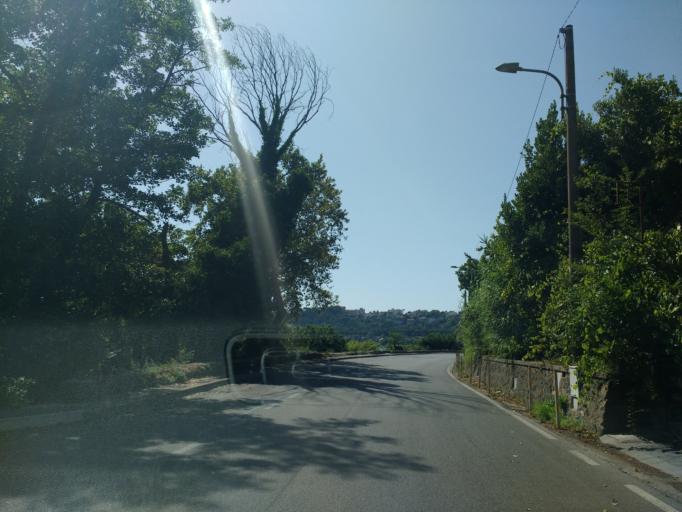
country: IT
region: Latium
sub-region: Citta metropolitana di Roma Capitale
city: Castel Gandolfo
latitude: 41.7592
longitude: 12.6683
